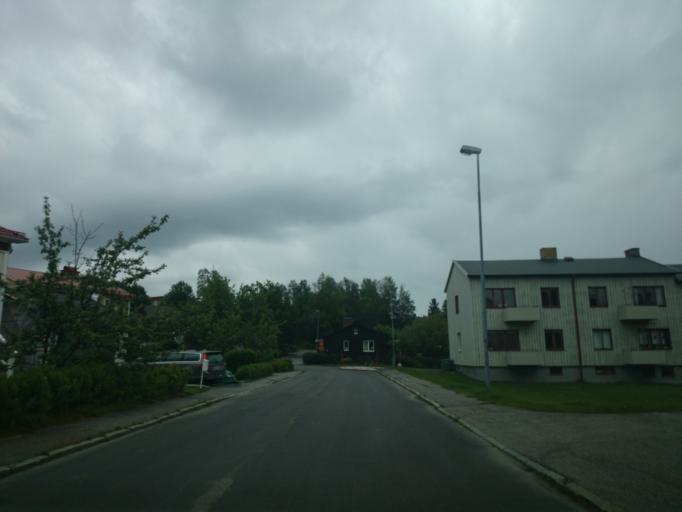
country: SE
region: Vaesternorrland
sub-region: Haernoesands Kommun
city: Haernoesand
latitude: 62.6398
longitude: 17.9221
